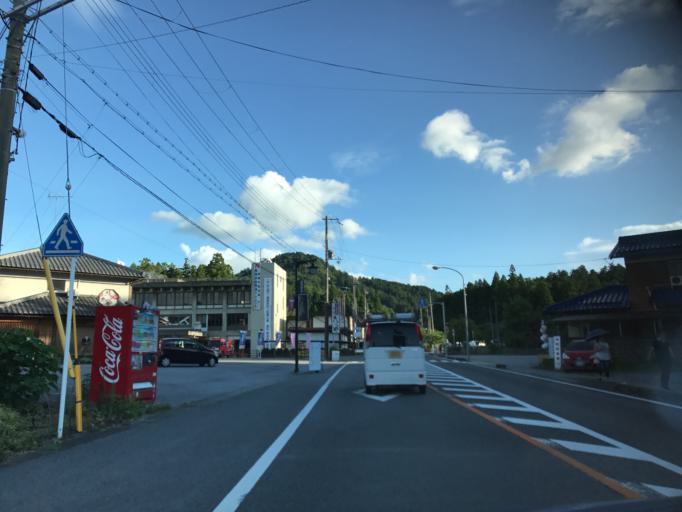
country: JP
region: Shiga Prefecture
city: Hikone
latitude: 35.2232
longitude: 136.2920
